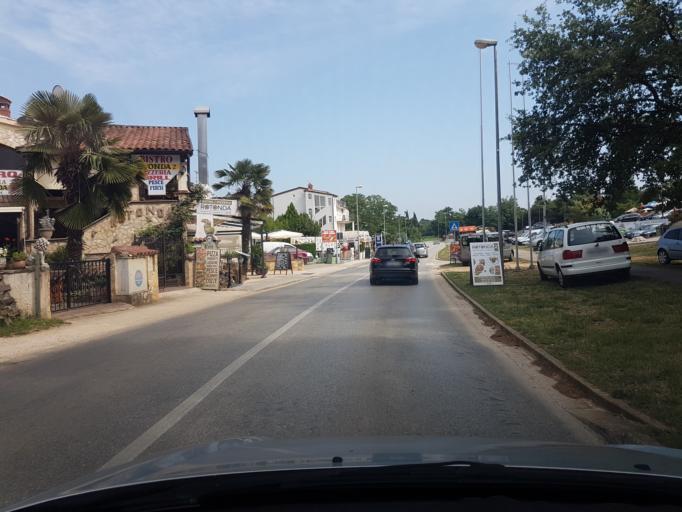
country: HR
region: Istarska
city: Vrsar
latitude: 45.1706
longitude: 13.6079
